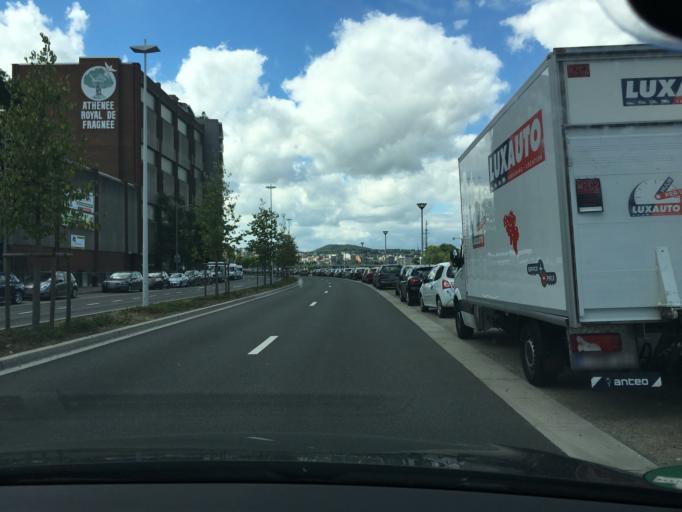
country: BE
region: Wallonia
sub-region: Province de Liege
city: Liege
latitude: 50.6238
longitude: 5.5764
